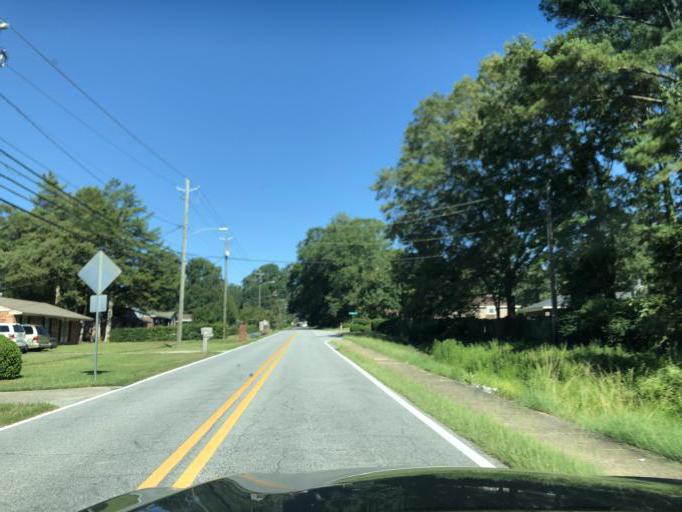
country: US
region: Georgia
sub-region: Muscogee County
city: Columbus
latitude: 32.5068
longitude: -84.9207
